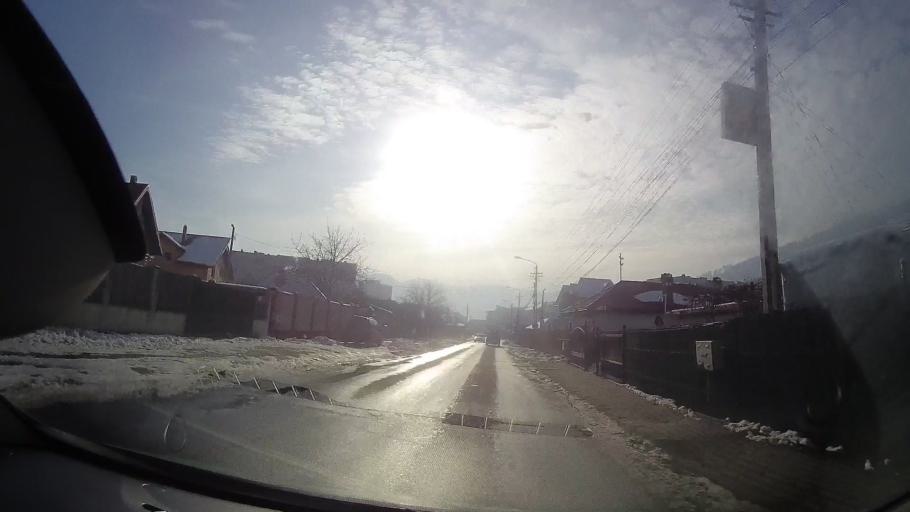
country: RO
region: Neamt
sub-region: Municipiul Piatra-Neamt
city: Valeni
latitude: 46.9460
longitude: 26.3839
